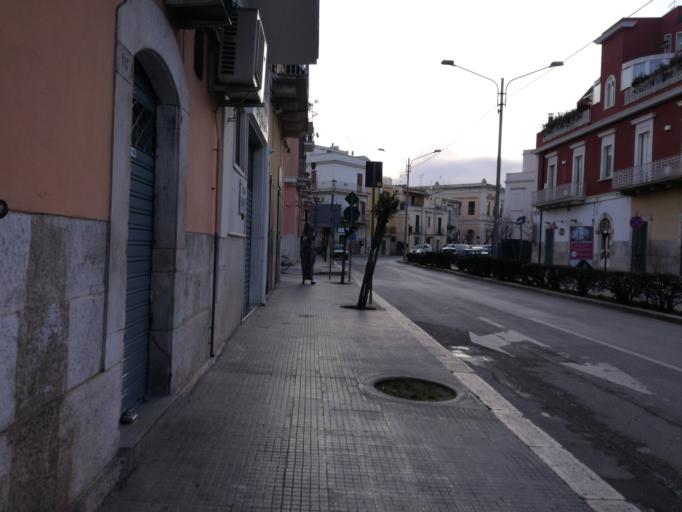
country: IT
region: Apulia
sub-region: Provincia di Bari
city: Corato
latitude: 41.1490
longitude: 16.4130
